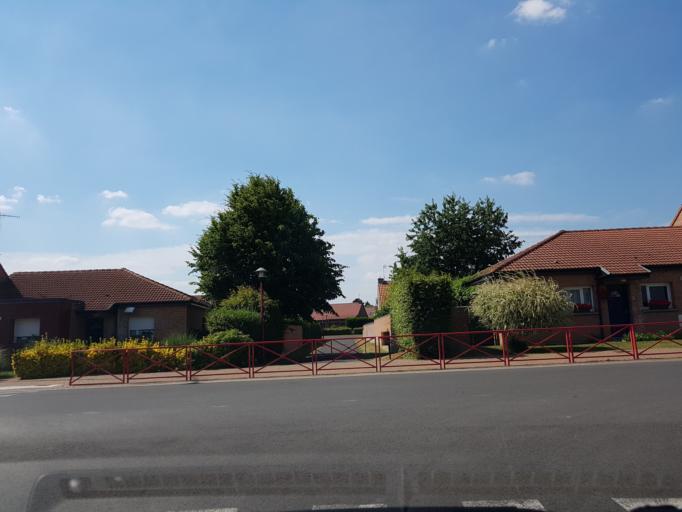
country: FR
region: Nord-Pas-de-Calais
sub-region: Departement du Nord
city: Roeulx
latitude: 50.3067
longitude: 3.3299
